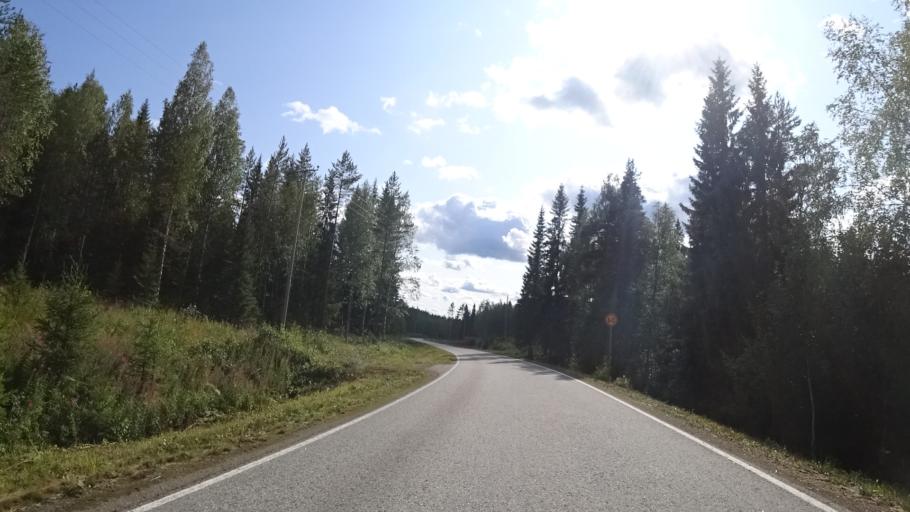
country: RU
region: Republic of Karelia
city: Vyartsilya
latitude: 62.2608
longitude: 30.7669
